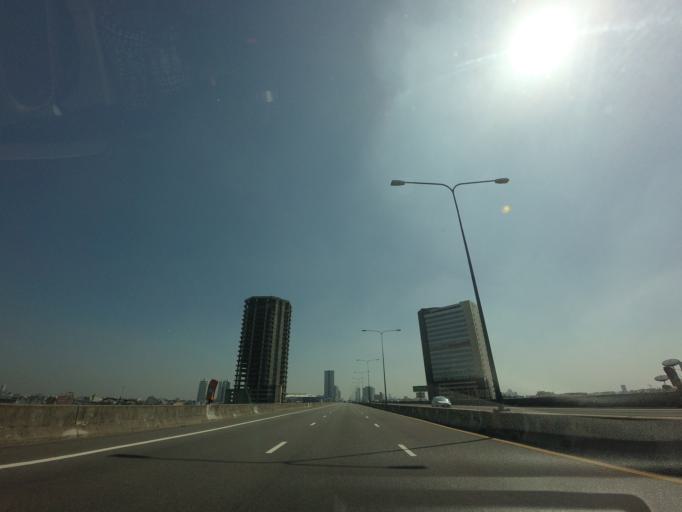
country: TH
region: Bangkok
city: Bang Na
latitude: 13.6705
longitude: 100.6210
